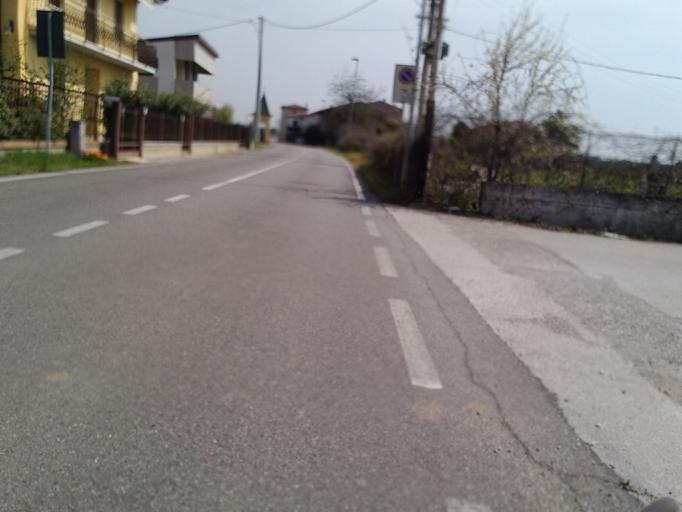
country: IT
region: Veneto
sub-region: Provincia di Verona
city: Sommacampagna
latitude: 45.4162
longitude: 10.8649
